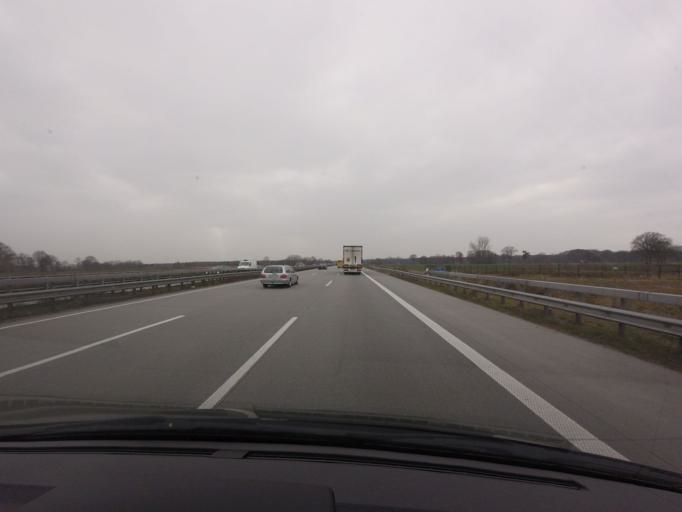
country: DE
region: Lower Saxony
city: Gyhum
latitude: 53.2089
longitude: 9.3080
